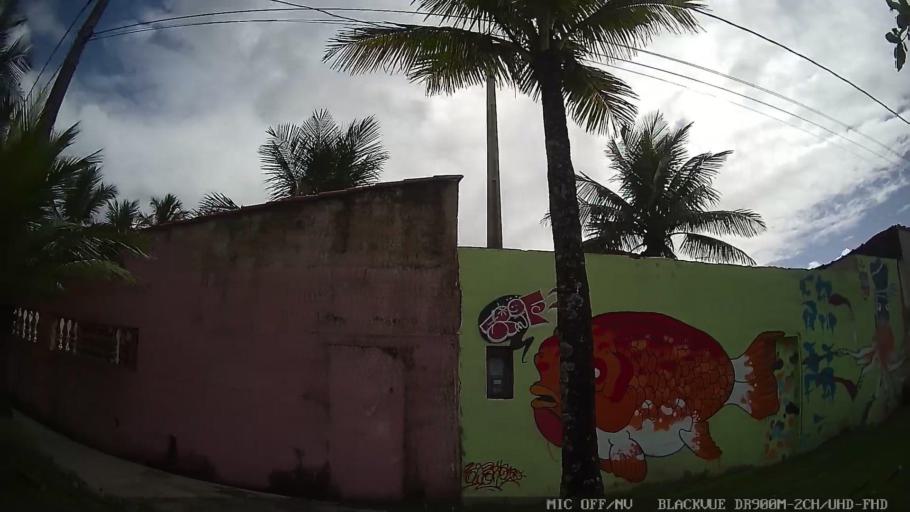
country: BR
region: Sao Paulo
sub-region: Itanhaem
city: Itanhaem
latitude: -24.1433
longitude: -46.7105
